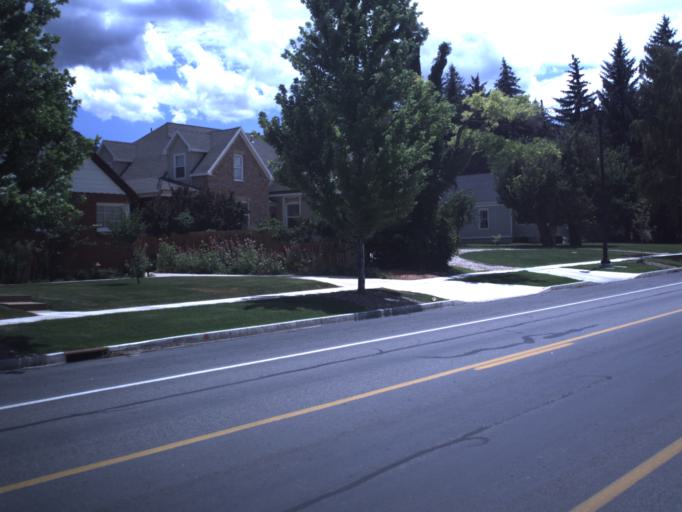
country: US
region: Utah
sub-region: Iron County
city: Parowan
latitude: 37.8401
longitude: -112.8276
